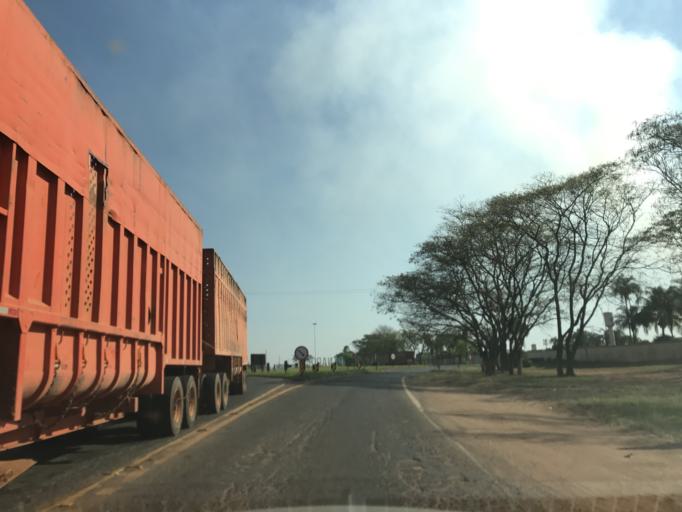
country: BR
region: Sao Paulo
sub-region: Penapolis
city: Penapolis
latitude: -21.3954
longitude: -50.1058
